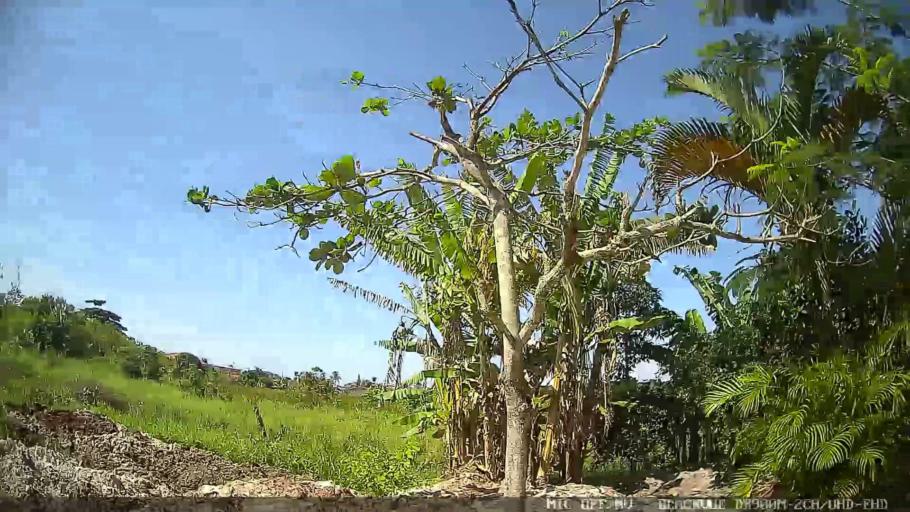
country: BR
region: Sao Paulo
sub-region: Itanhaem
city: Itanhaem
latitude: -24.2116
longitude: -46.8551
